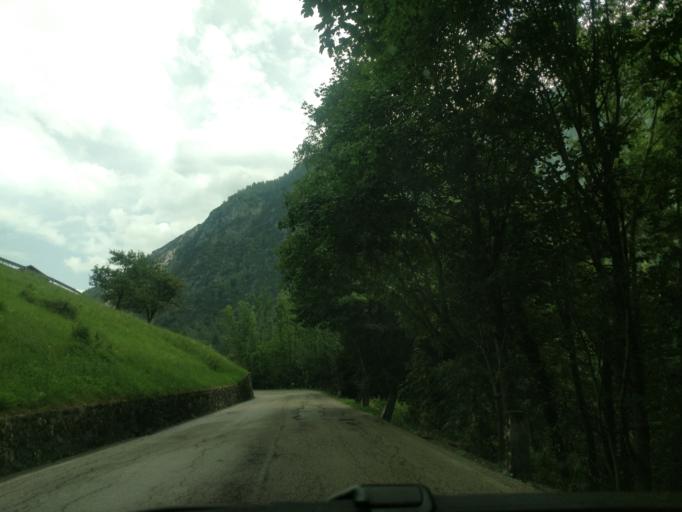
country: IT
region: Veneto
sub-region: Provincia di Belluno
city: Rivamonte Agordino
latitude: 46.2247
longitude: 12.0004
